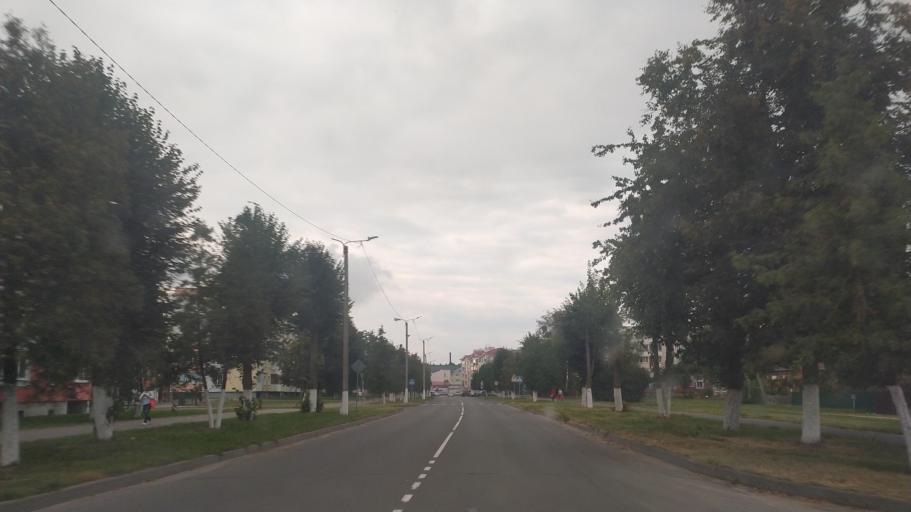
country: BY
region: Brest
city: Byaroza
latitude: 52.5310
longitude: 24.9862
